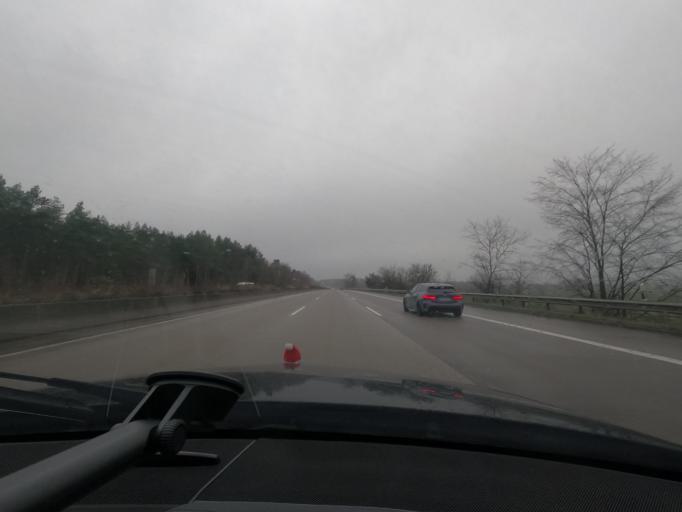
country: DE
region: Lower Saxony
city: Garlstorf
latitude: 53.2440
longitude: 10.0830
